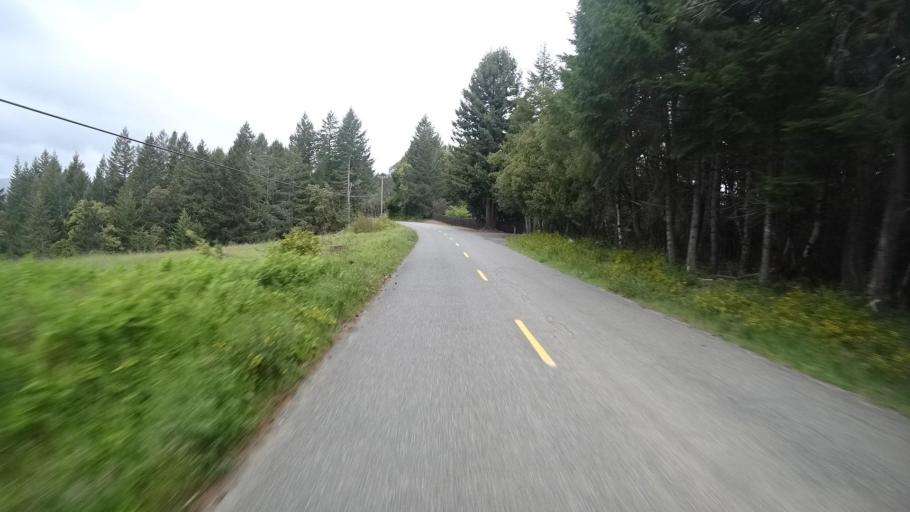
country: US
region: California
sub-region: Humboldt County
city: Redway
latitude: 40.2927
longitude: -123.8164
